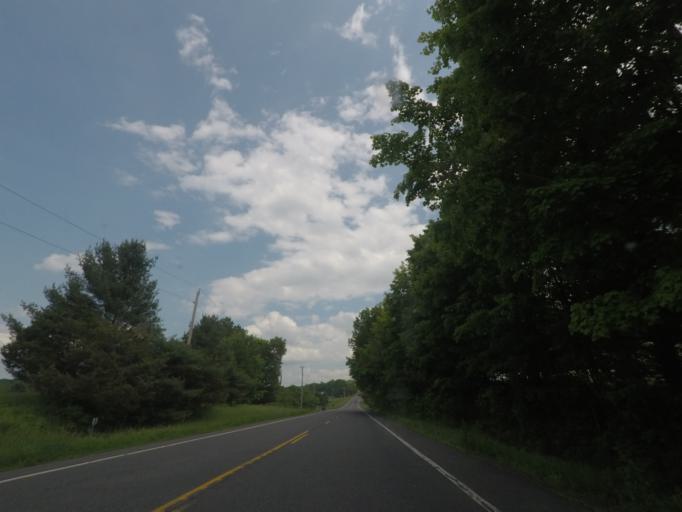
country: US
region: New York
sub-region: Dutchess County
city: Pine Plains
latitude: 42.1136
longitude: -73.7080
